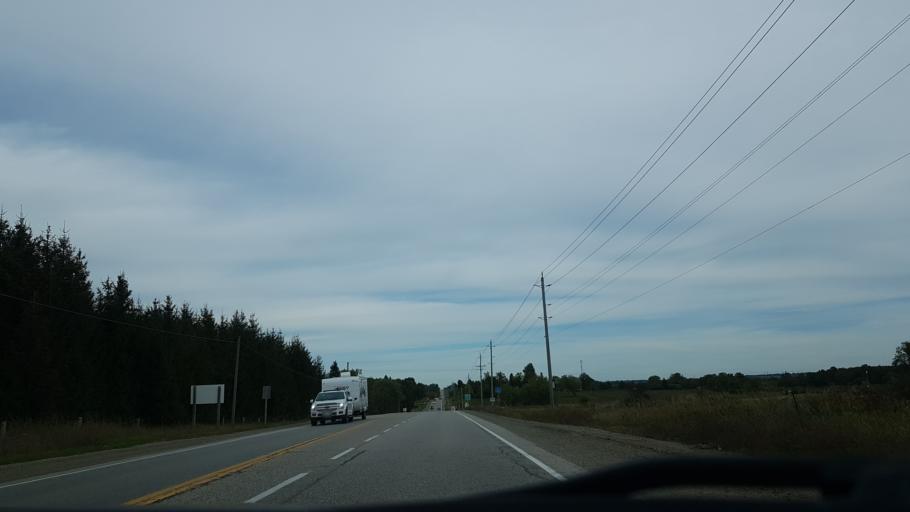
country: CA
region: Ontario
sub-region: Wellington County
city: Guelph
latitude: 43.6765
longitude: -80.1569
